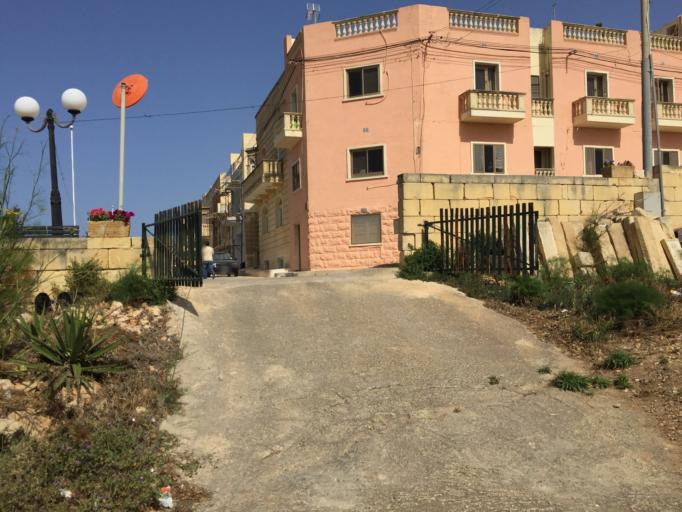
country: MT
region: Il-Fontana
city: Fontana
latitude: 36.0345
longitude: 14.2356
